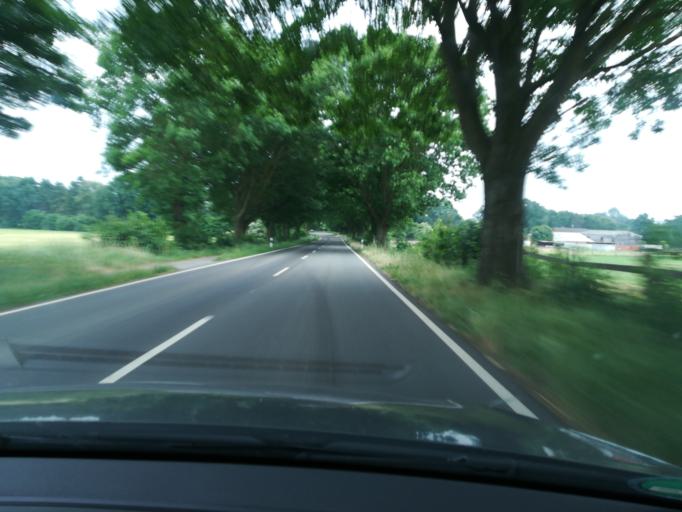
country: DE
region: Schleswig-Holstein
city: Grossensee
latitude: 53.6232
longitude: 10.3307
